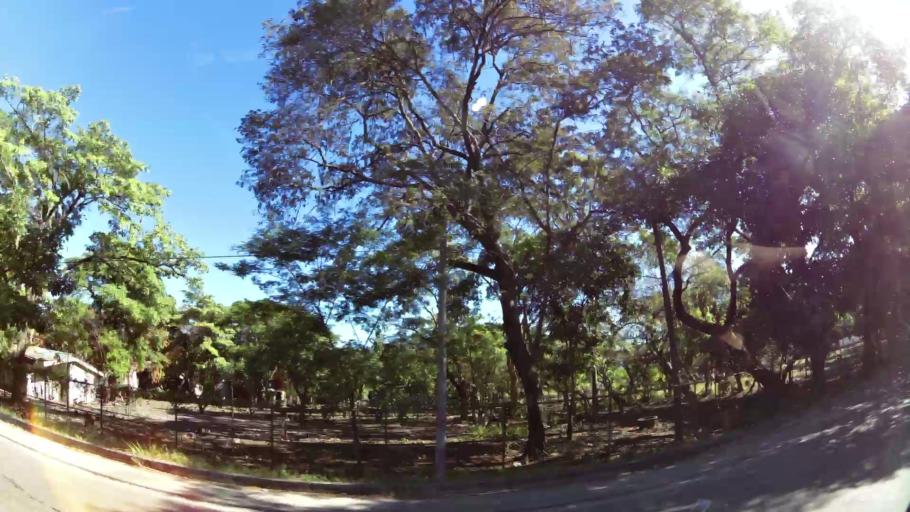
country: SV
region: San Miguel
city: San Miguel
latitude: 13.4543
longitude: -88.1410
